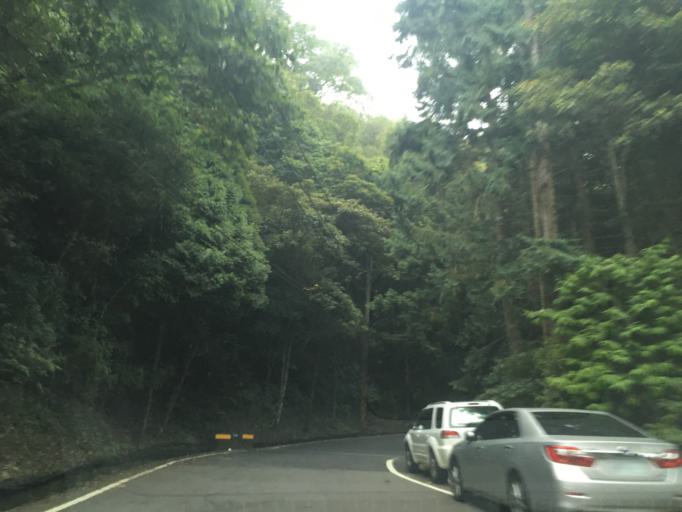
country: TW
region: Taiwan
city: Fengyuan
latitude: 24.2442
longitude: 120.9207
